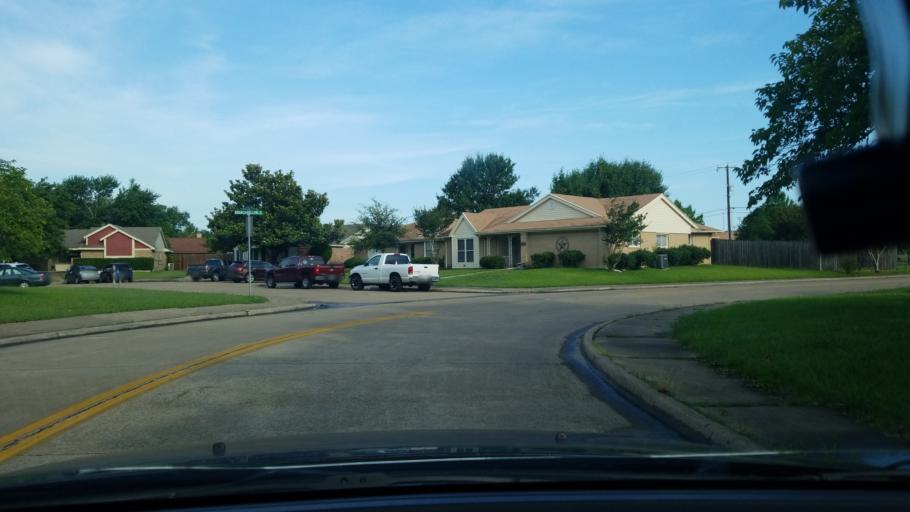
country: US
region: Texas
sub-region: Dallas County
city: Mesquite
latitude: 32.8044
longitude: -96.6031
